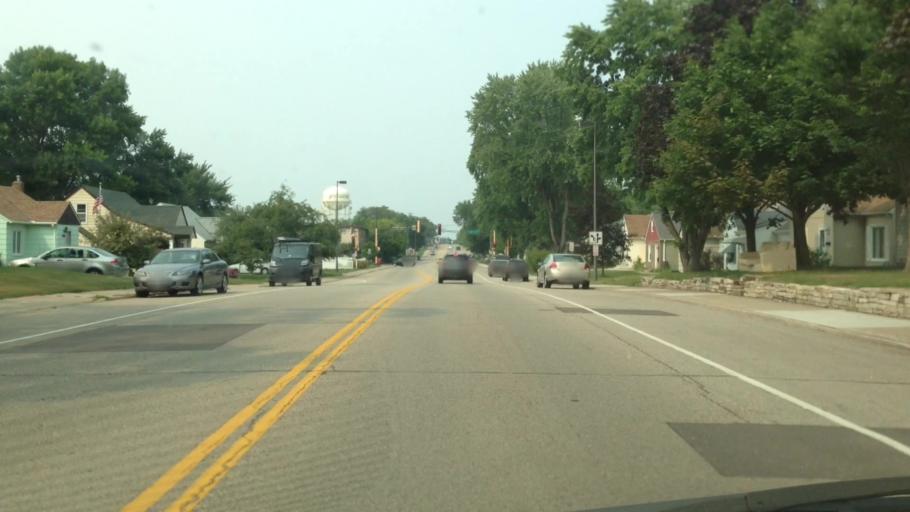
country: US
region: Minnesota
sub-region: Hennepin County
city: Saint Louis Park
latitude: 44.9517
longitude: -93.3708
